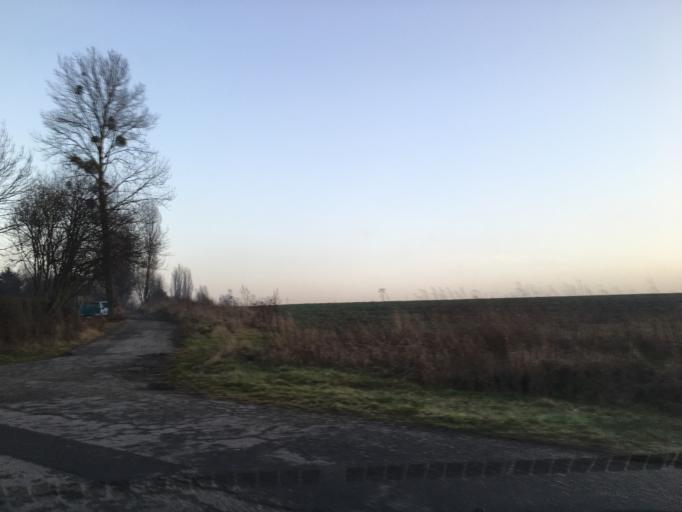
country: PL
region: Silesian Voivodeship
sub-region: Powiat tarnogorski
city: Radzionkow
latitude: 50.3672
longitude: 18.8890
